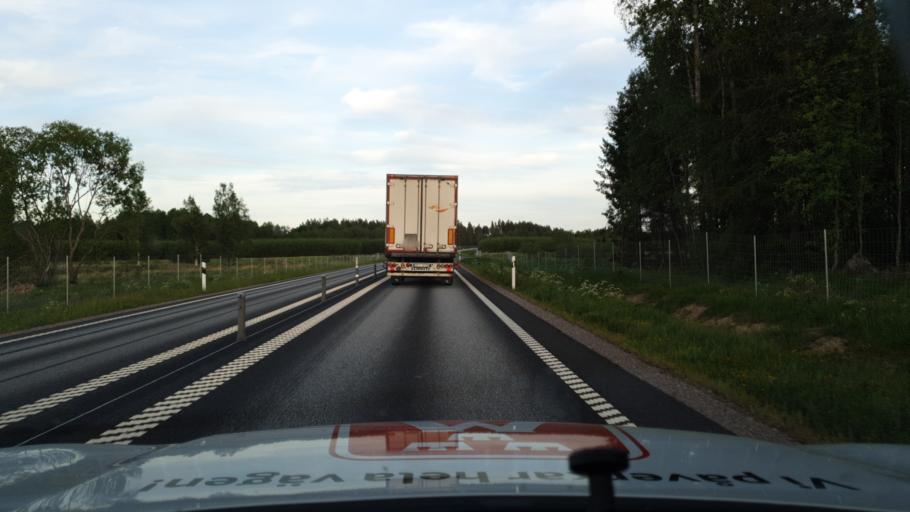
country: SE
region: OErebro
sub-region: Hallsbergs Kommun
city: Palsboda
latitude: 59.0448
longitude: 15.3441
